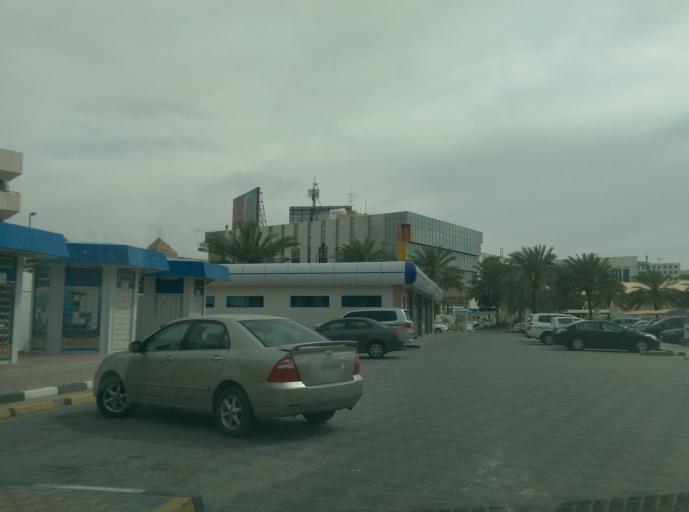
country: AE
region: Ash Shariqah
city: Sharjah
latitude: 25.2449
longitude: 55.3100
